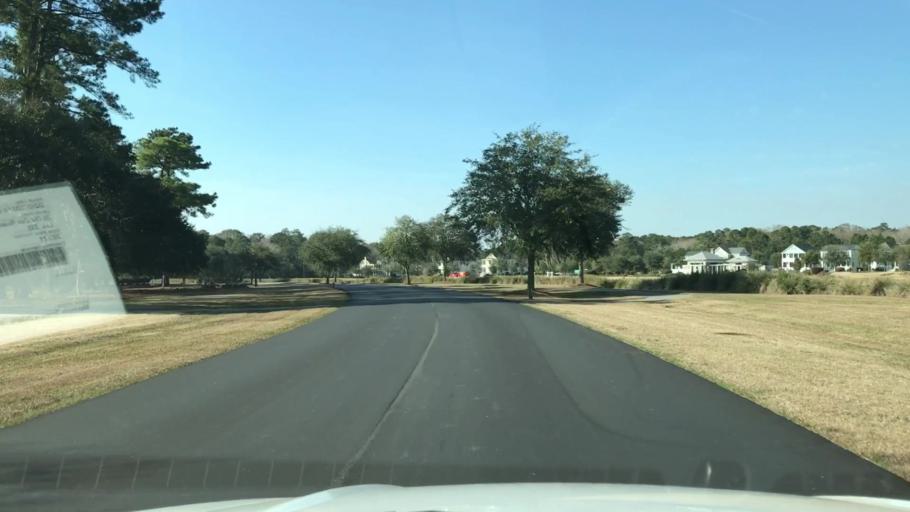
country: US
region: South Carolina
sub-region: Beaufort County
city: Bluffton
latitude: 32.3408
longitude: -80.9122
